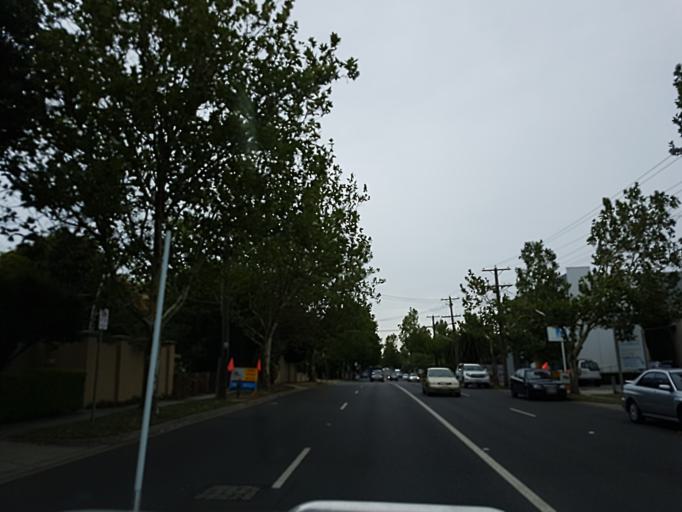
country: AU
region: Victoria
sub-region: Boroondara
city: Canterbury
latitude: -37.8253
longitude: 145.0922
